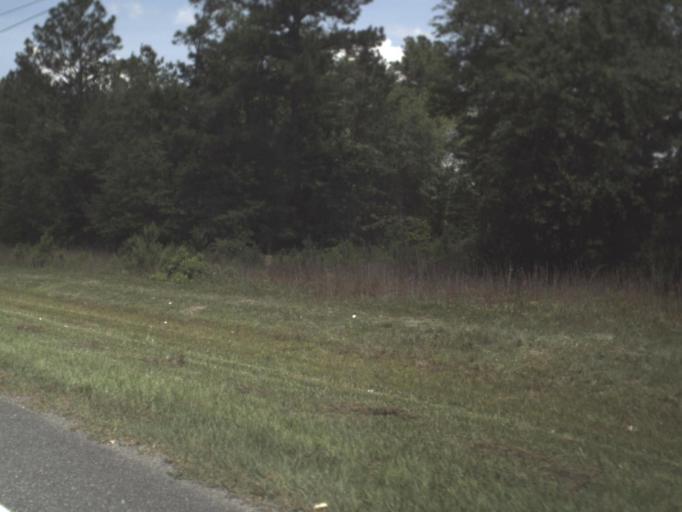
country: US
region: Florida
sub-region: Union County
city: Lake Butler
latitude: 29.9890
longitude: -82.2580
